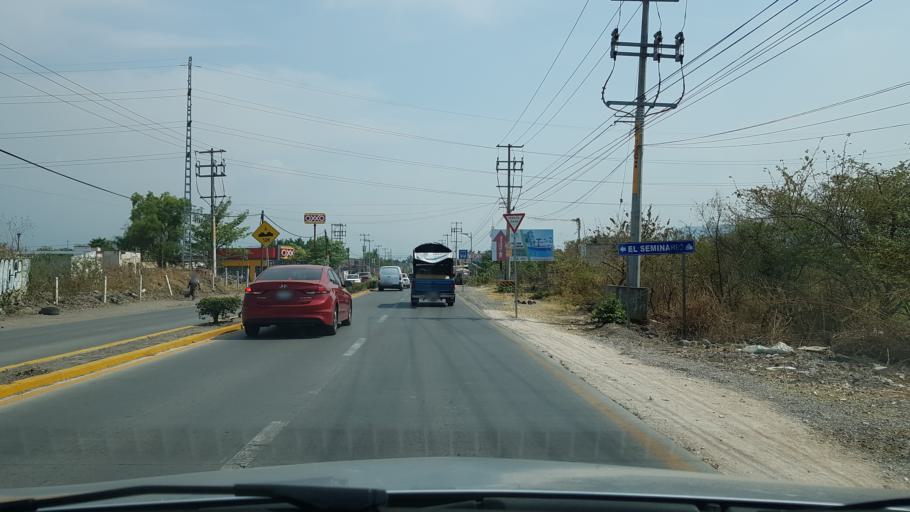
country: MX
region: Morelos
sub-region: Xochitepec
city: Chiconcuac
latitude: 18.8088
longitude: -99.1945
